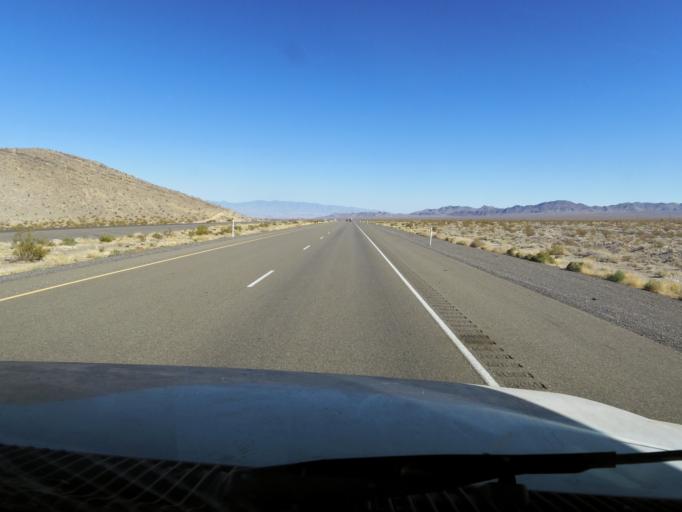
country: US
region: Nevada
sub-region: Nye County
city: Pahrump
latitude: 36.5707
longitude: -115.8595
